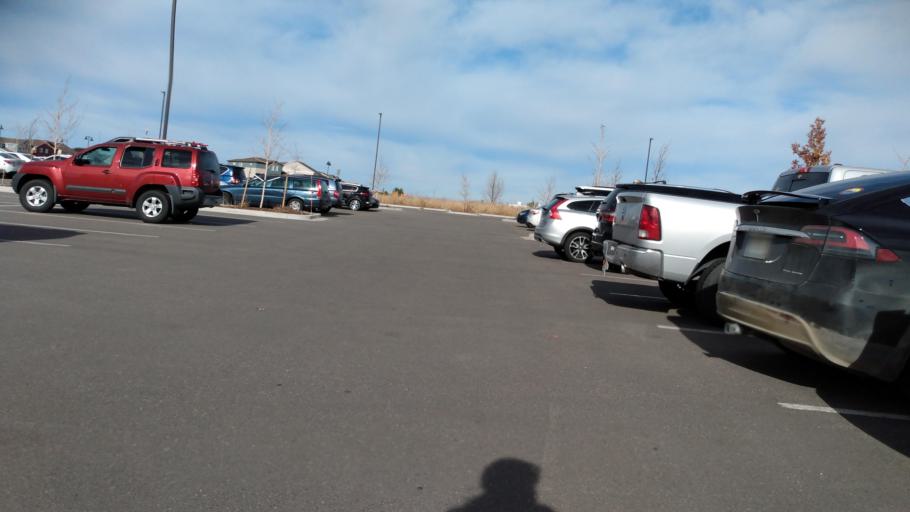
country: US
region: Colorado
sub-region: Boulder County
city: Erie
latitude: 40.0031
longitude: -104.9931
